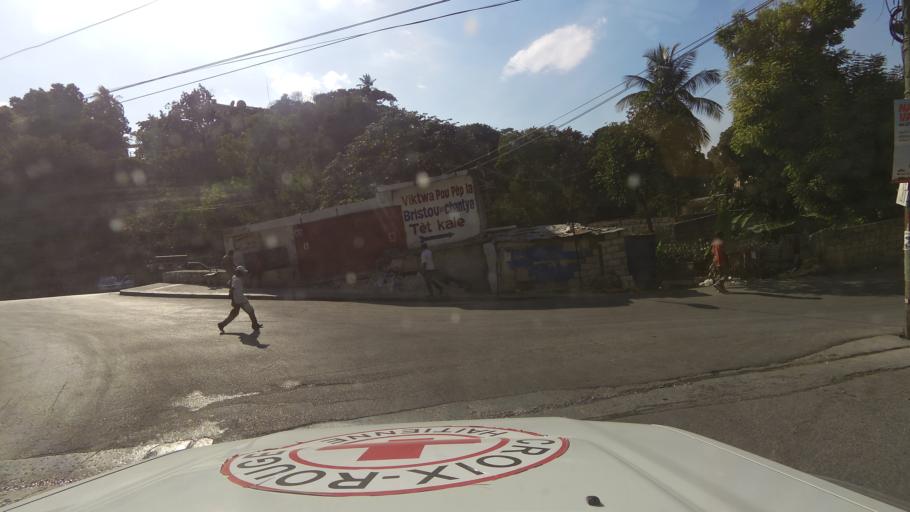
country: HT
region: Ouest
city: Petionville
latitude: 18.5146
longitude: -72.2750
